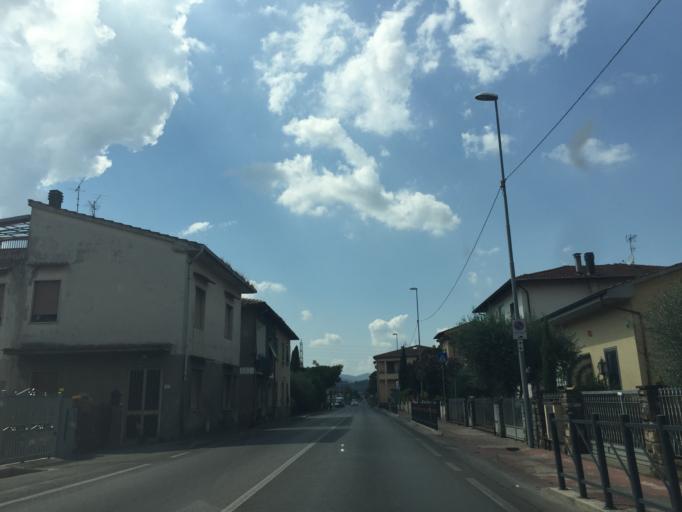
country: IT
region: Tuscany
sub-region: Provincia di Prato
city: Poggio A Caiano
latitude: 43.8123
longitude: 11.0742
